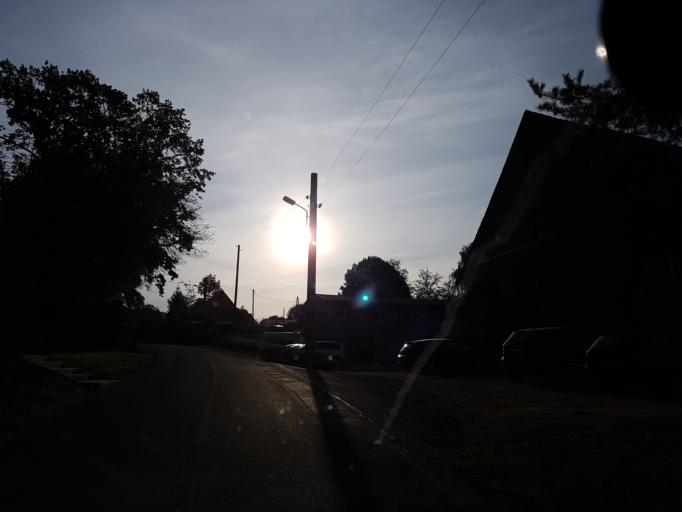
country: DE
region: Saxony
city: Dobeln
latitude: 51.1155
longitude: 13.0752
